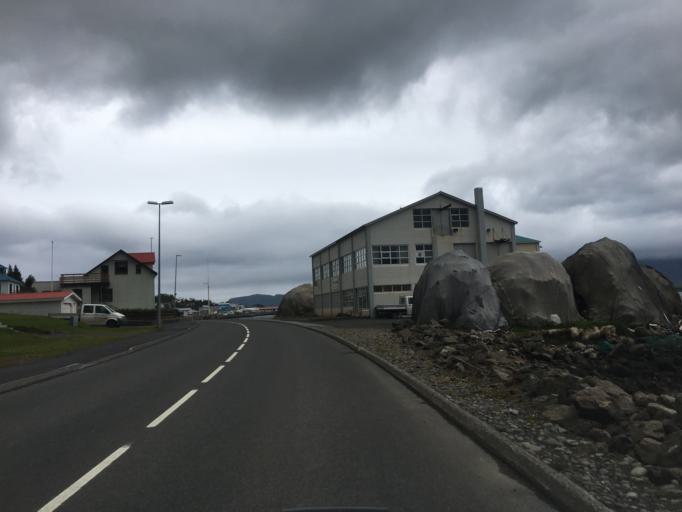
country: IS
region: East
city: Neskaupstadur
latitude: 65.1474
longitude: -13.7059
